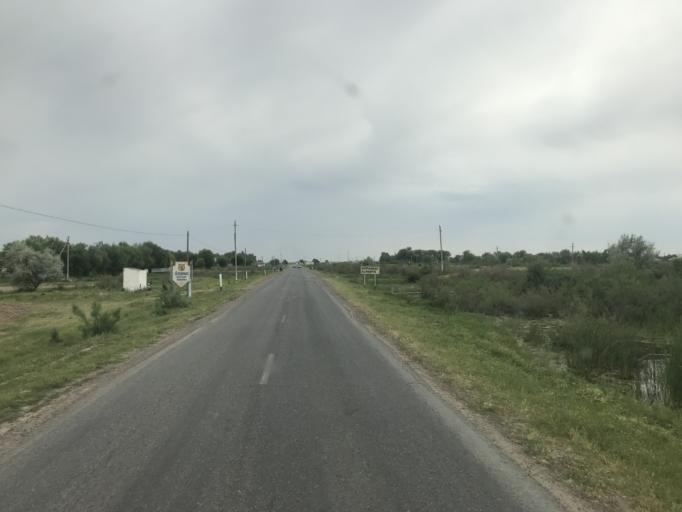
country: KZ
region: Ongtustik Qazaqstan
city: Asykata
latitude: 40.9161
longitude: 68.3964
